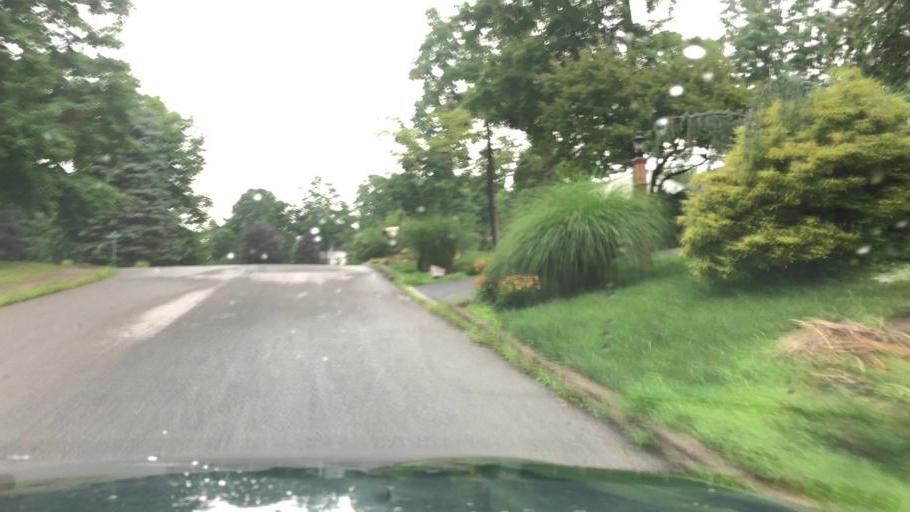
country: US
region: New York
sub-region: Dutchess County
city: Fishkill
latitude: 41.5320
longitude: -73.9178
